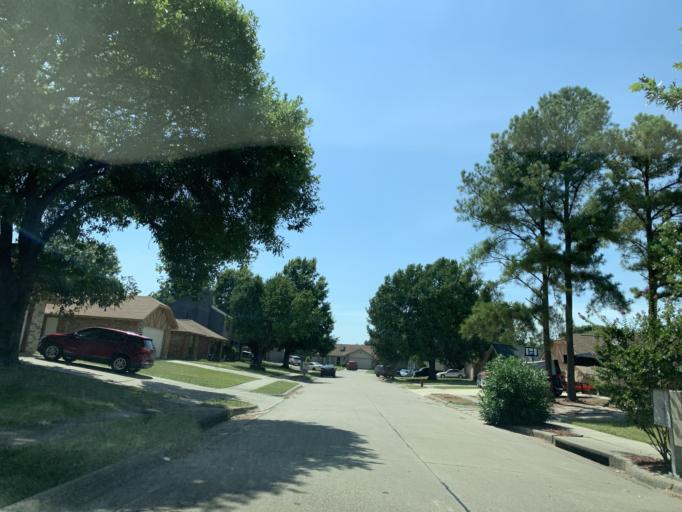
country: US
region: Texas
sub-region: Dallas County
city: Cedar Hill
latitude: 32.6514
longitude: -97.0156
